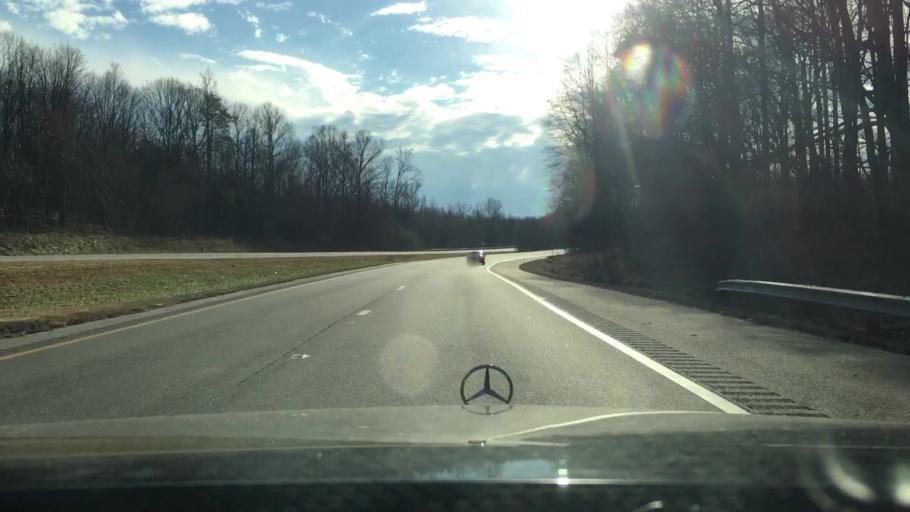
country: US
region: Virginia
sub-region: City of Danville
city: Danville
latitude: 36.5506
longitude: -79.3925
